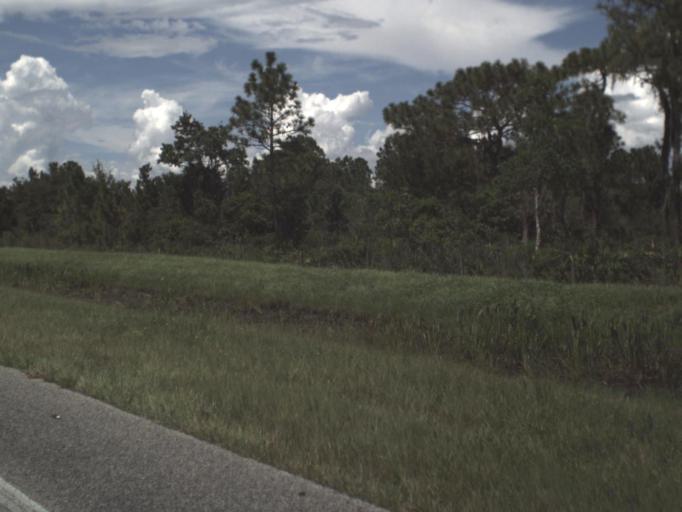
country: US
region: Florida
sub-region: Polk County
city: Babson Park
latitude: 27.8180
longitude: -81.3299
